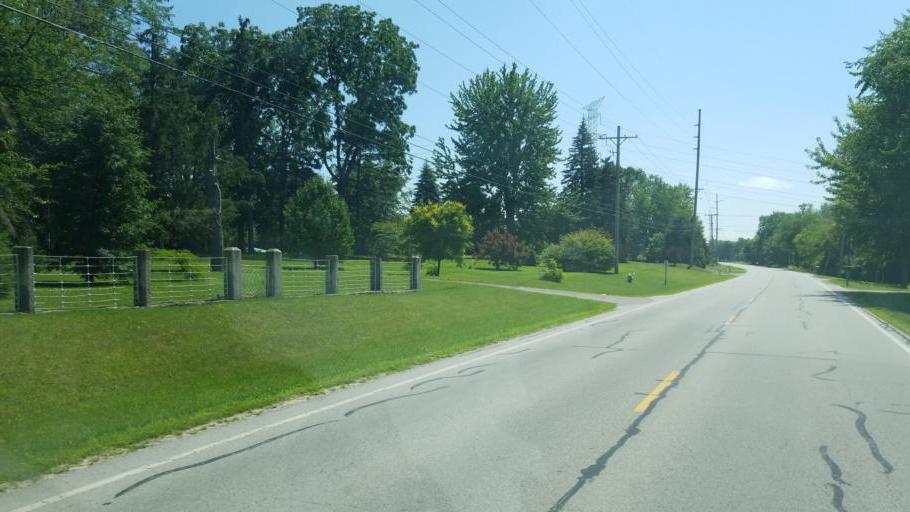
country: US
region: Ohio
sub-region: Huron County
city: Bellevue
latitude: 41.3885
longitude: -82.8129
